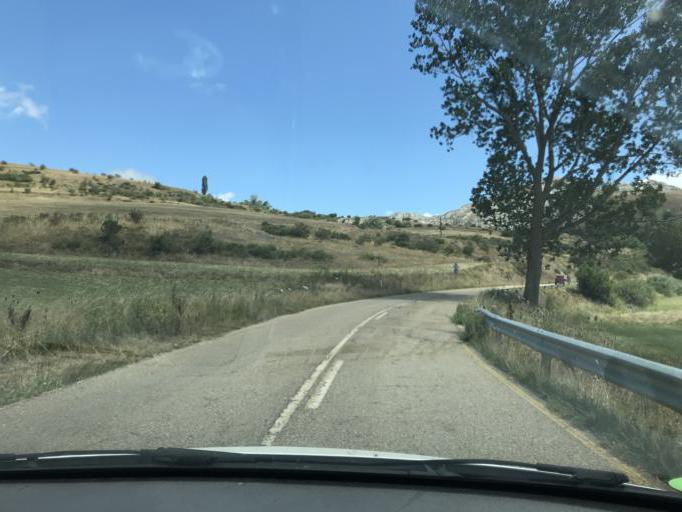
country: ES
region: Castille and Leon
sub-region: Provincia de Palencia
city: Polentinos
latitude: 43.0130
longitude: -4.4953
